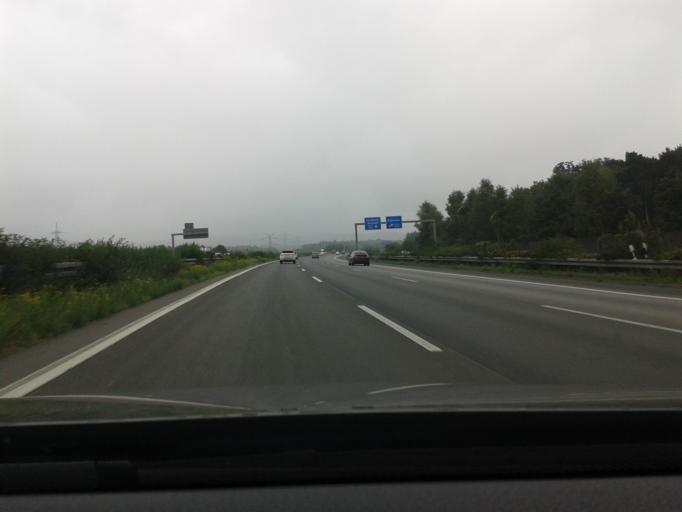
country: DE
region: North Rhine-Westphalia
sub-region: Regierungsbezirk Detmold
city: Verl
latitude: 51.9408
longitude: 8.5392
